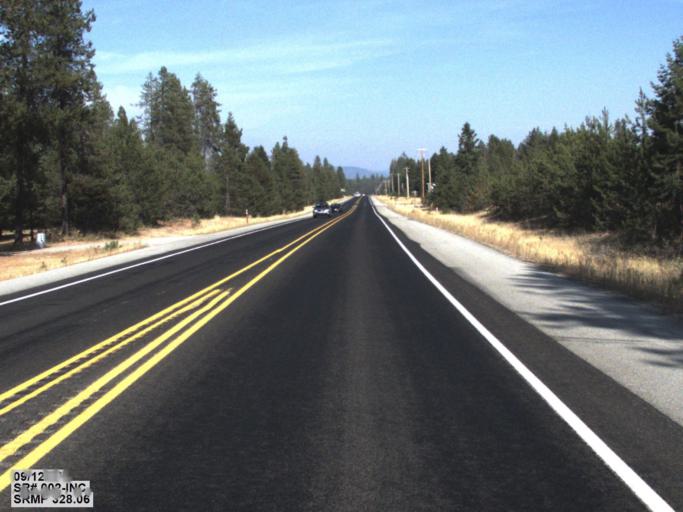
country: US
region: Washington
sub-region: Pend Oreille County
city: Newport
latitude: 48.1418
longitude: -117.1538
